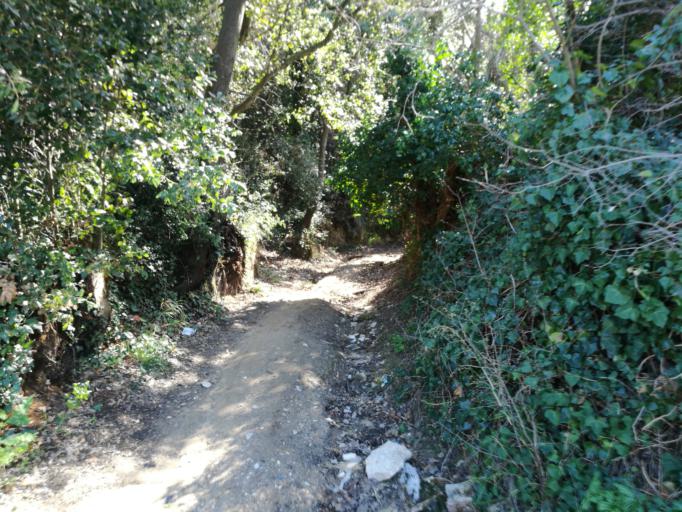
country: IT
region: Molise
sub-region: Provincia di Campobasso
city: Termoli
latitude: 41.9845
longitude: 14.9784
